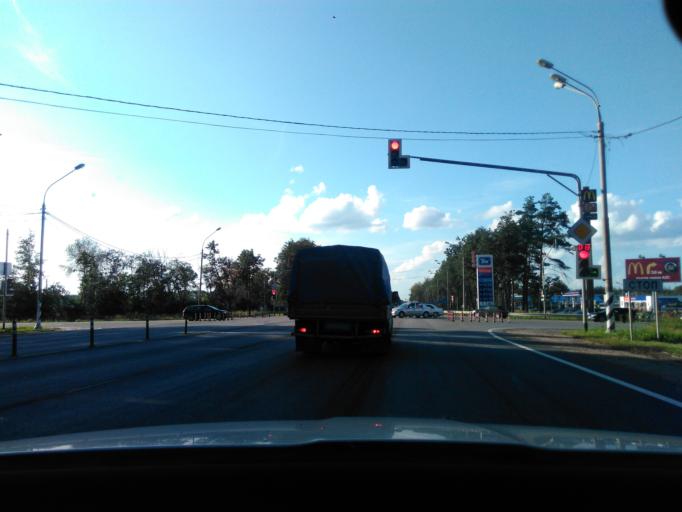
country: RU
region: Tverskaya
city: Zavidovo
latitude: 56.5732
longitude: 36.4995
